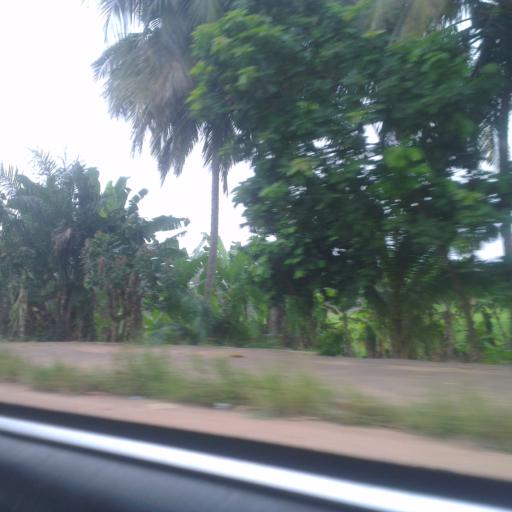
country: CI
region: Vallee du Bandama
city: Bouake
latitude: 7.6824
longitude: -5.0502
